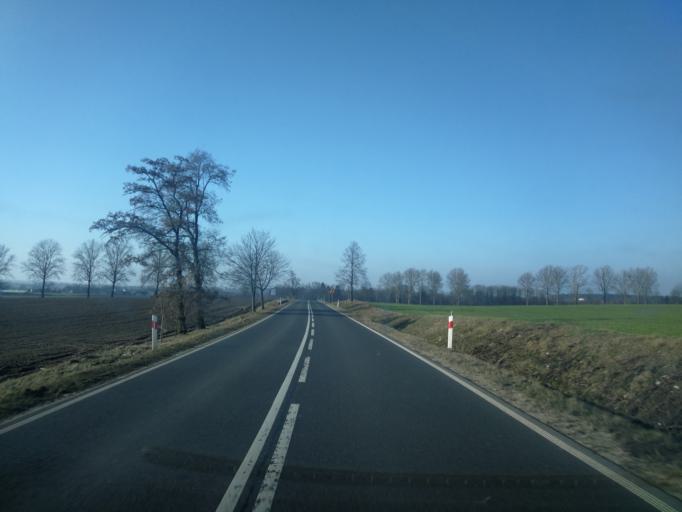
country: PL
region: Warmian-Masurian Voivodeship
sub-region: Powiat ilawski
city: Lubawa
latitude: 53.4177
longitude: 19.7887
